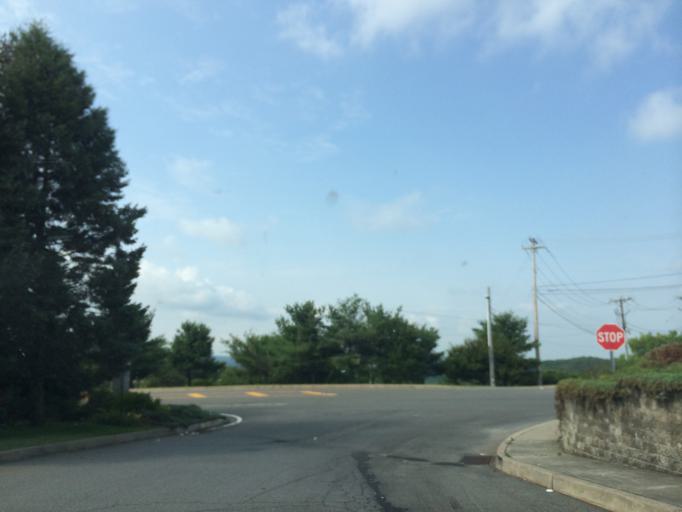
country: US
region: Pennsylvania
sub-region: Lackawanna County
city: Taylor
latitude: 41.3705
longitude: -75.6824
